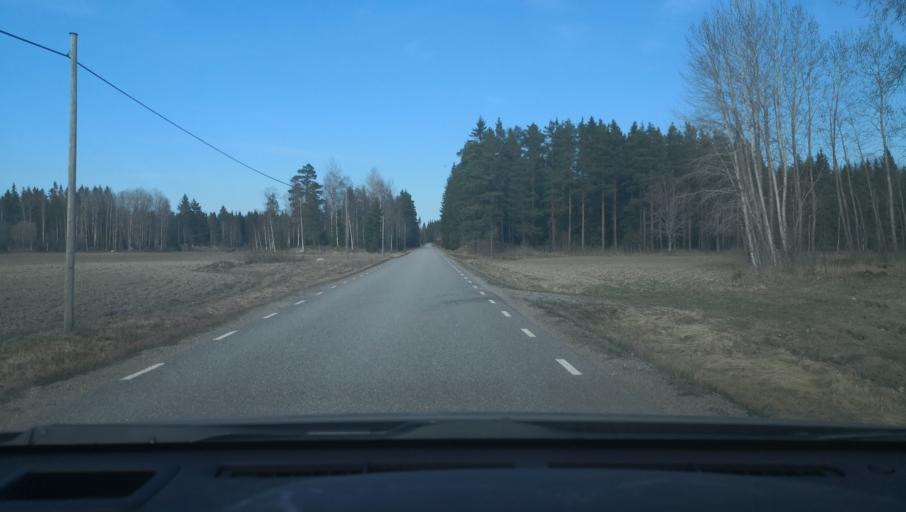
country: SE
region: Uppsala
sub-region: Heby Kommun
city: Heby
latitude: 59.9106
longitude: 16.8255
